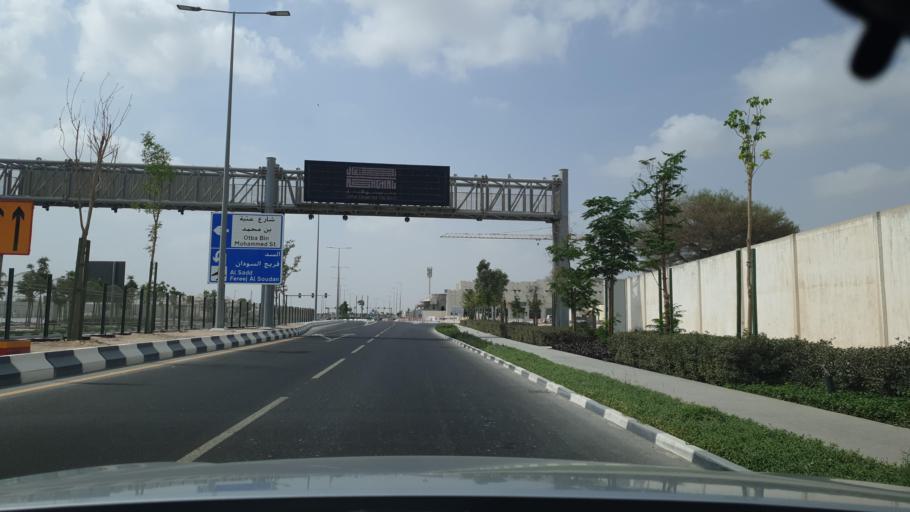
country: QA
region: Baladiyat ar Rayyan
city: Ar Rayyan
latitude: 25.2783
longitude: 51.4652
